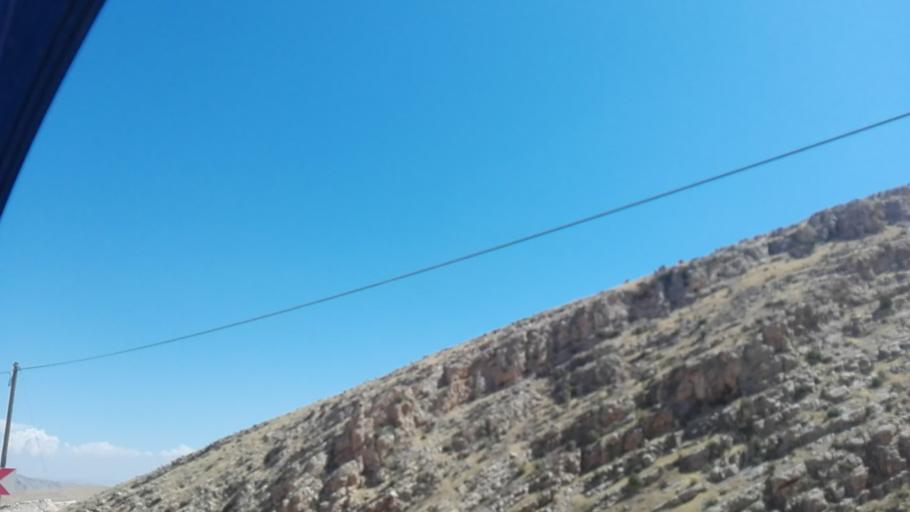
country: TR
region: Batman
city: Hasankeyf
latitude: 37.7005
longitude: 41.4602
